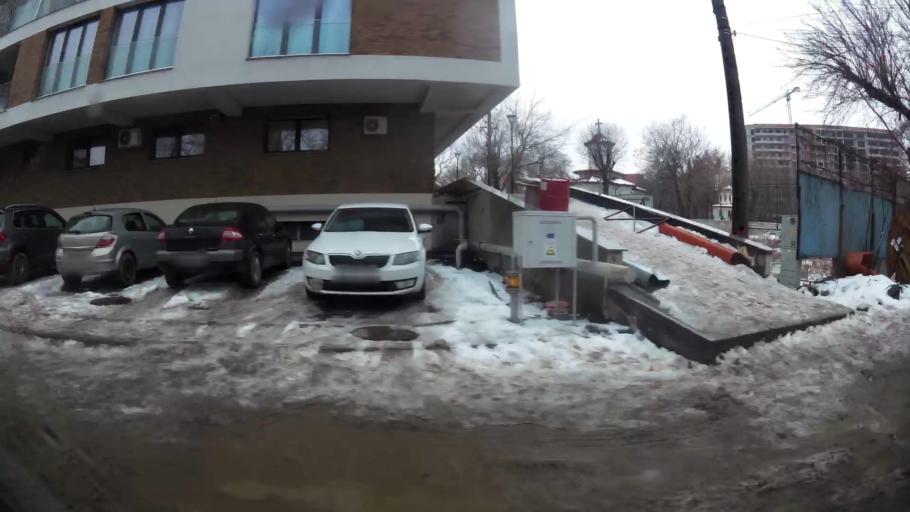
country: RO
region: Ilfov
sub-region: Comuna Chiajna
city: Rosu
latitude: 44.4411
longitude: 26.0543
